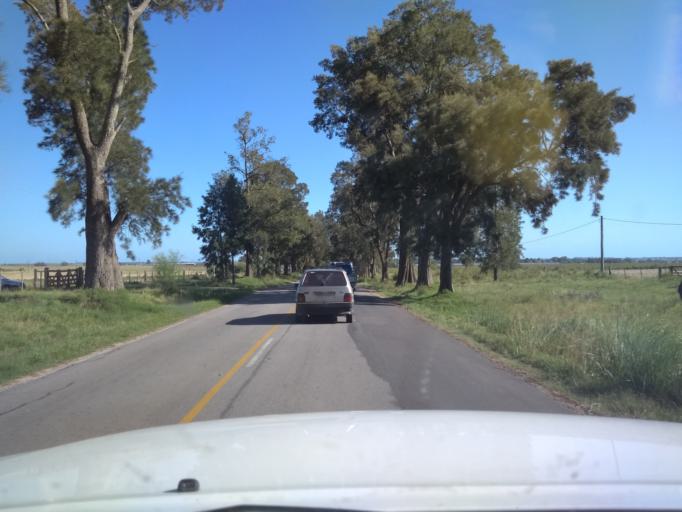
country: UY
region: Canelones
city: San Bautista
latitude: -34.3961
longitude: -55.9596
